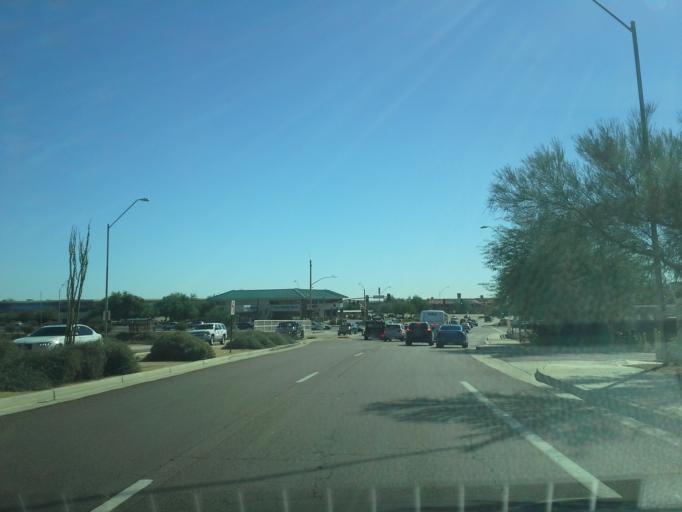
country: US
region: Arizona
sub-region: Maricopa County
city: Paradise Valley
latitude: 33.6358
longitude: -111.9076
